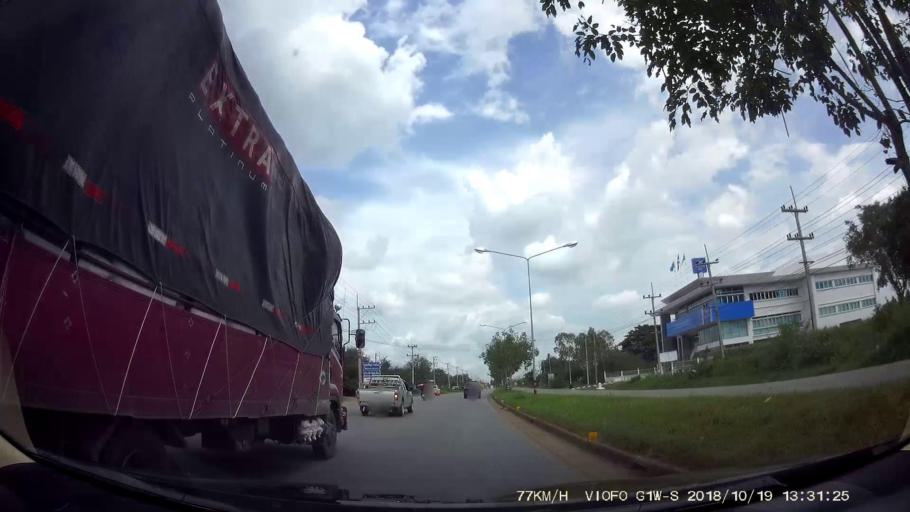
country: TH
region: Chaiyaphum
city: Chatturat
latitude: 15.5771
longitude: 101.8672
